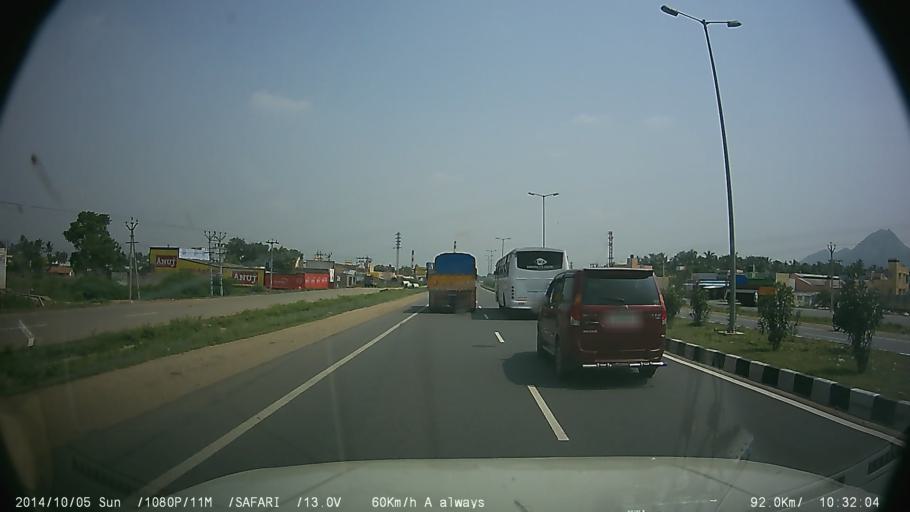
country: IN
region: Tamil Nadu
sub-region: Salem
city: Salem
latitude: 11.6333
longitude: 78.1680
